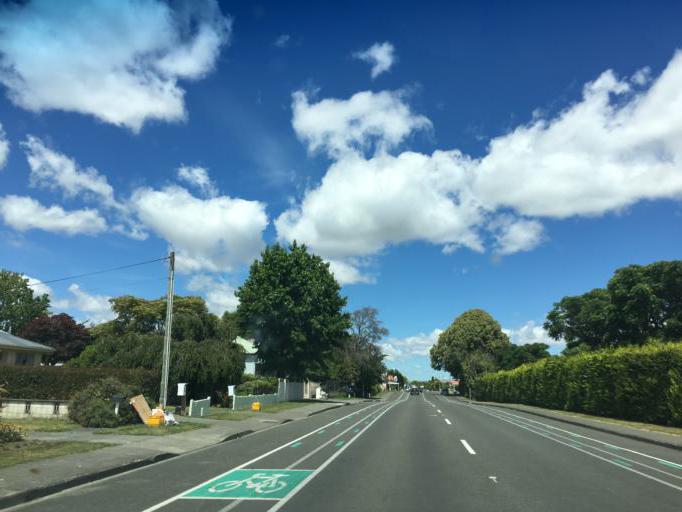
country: NZ
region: Hawke's Bay
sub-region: Hastings District
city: Hastings
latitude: -39.6485
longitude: 176.8625
